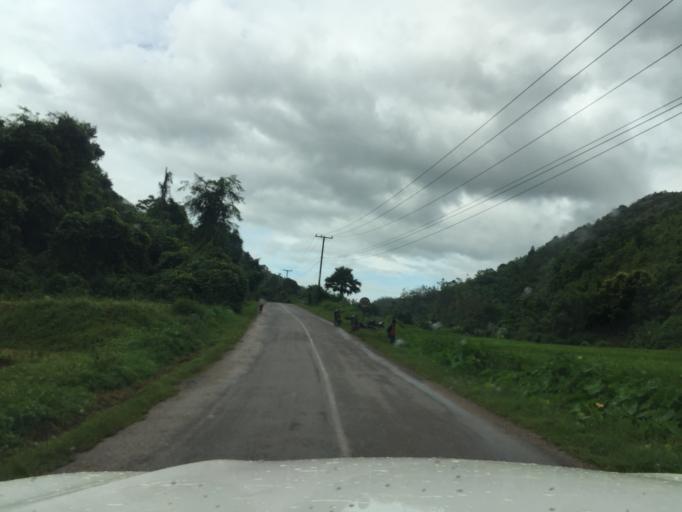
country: LA
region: Oudomxai
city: Muang La
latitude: 20.8185
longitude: 102.0933
